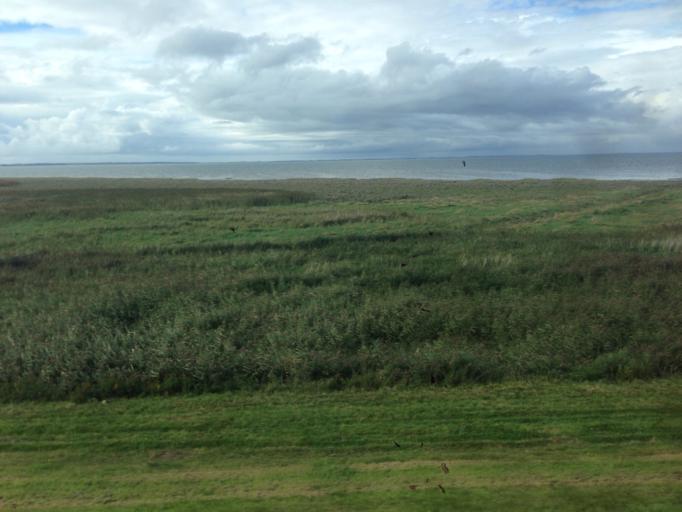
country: DE
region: Schleswig-Holstein
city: Sylt-Ost
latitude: 54.8753
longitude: 8.4865
